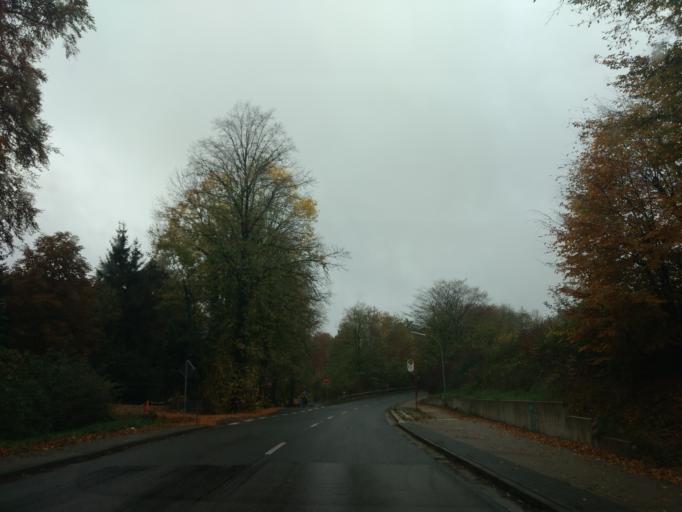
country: DE
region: Lower Saxony
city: Georgsmarienhutte
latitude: 52.2363
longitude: 8.0629
